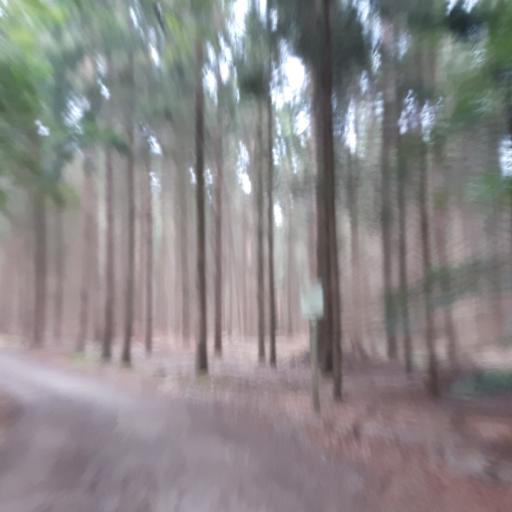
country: NL
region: Utrecht
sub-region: Gemeente Utrechtse Heuvelrug
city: Amerongen
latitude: 52.0045
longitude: 5.4938
